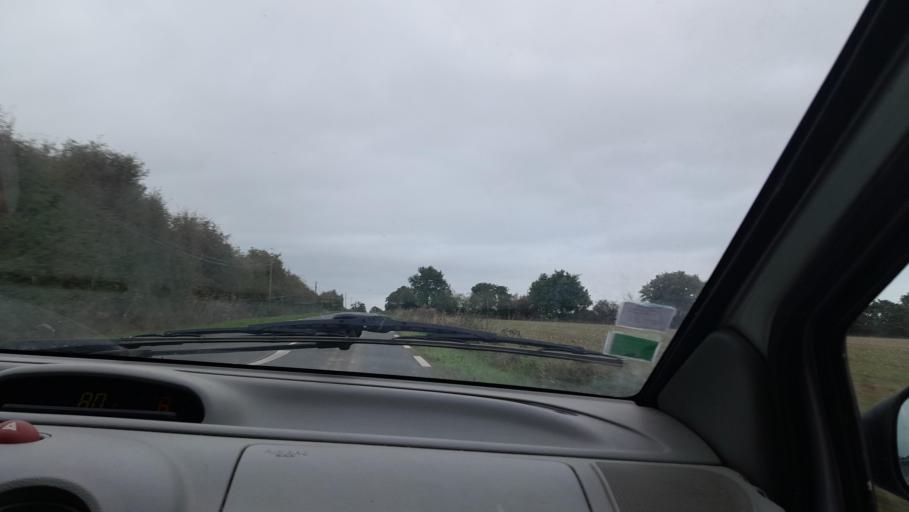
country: FR
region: Pays de la Loire
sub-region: Departement de la Loire-Atlantique
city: Saint-Mars-la-Jaille
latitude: 47.6298
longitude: -1.2006
